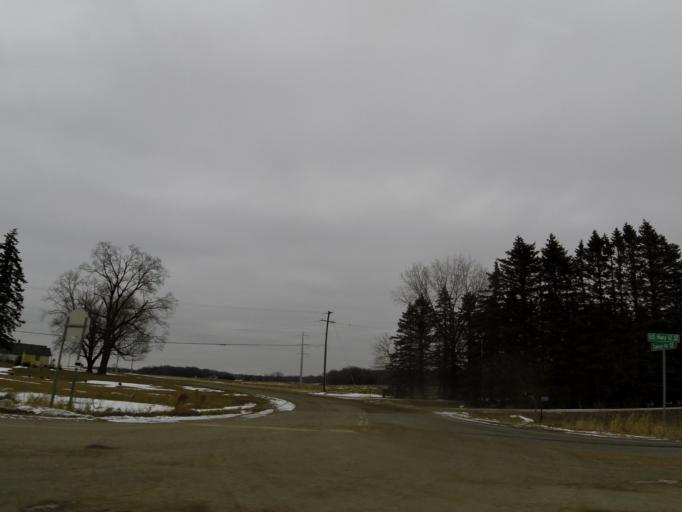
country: US
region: Minnesota
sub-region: Wright County
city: Delano
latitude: 45.0620
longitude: -93.8079
